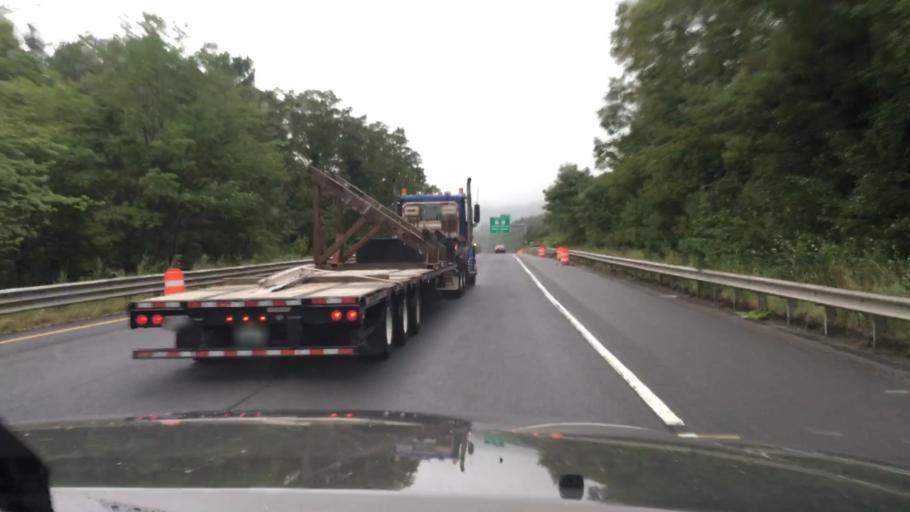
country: US
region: Massachusetts
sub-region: Franklin County
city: Greenfield
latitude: 42.6134
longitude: -72.6013
